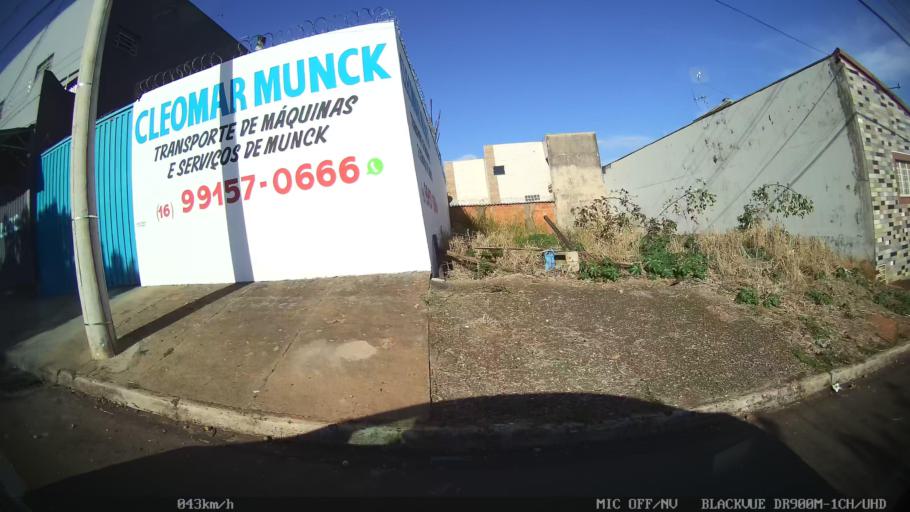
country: BR
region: Sao Paulo
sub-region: Franca
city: Franca
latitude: -20.5093
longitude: -47.4117
